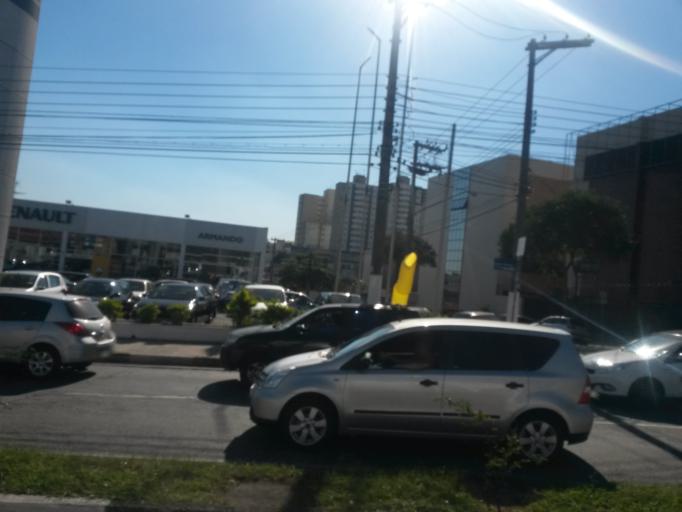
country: BR
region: Sao Paulo
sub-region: Santo Andre
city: Santo Andre
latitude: -23.6798
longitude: -46.5392
